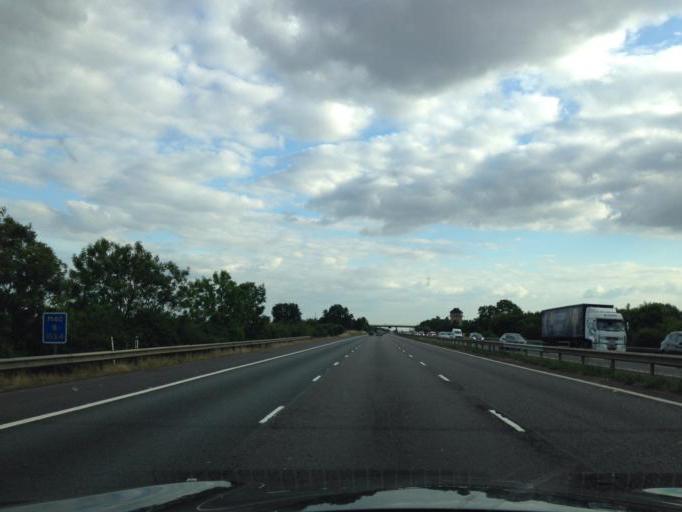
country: GB
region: England
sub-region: Oxfordshire
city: Bicester
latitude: 51.9232
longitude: -1.2023
